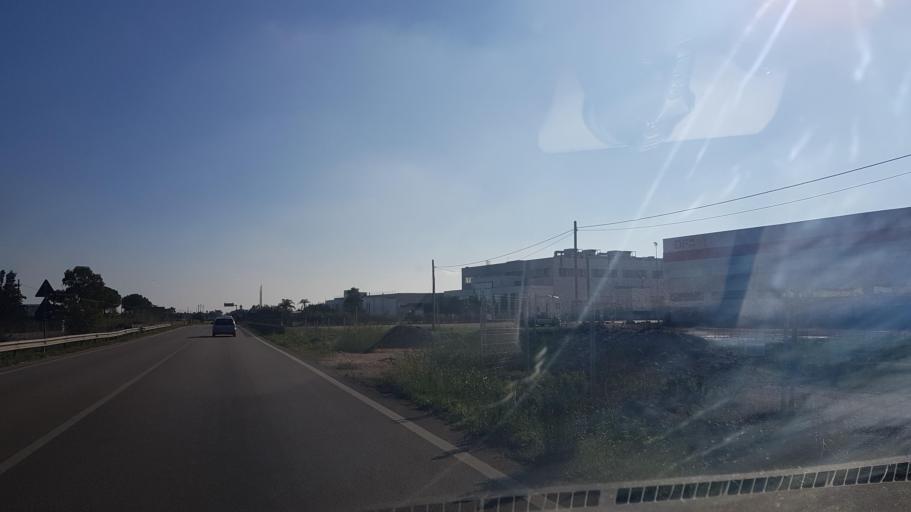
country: IT
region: Apulia
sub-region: Provincia di Lecce
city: Montesano Salentino
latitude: 40.0027
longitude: 18.3236
